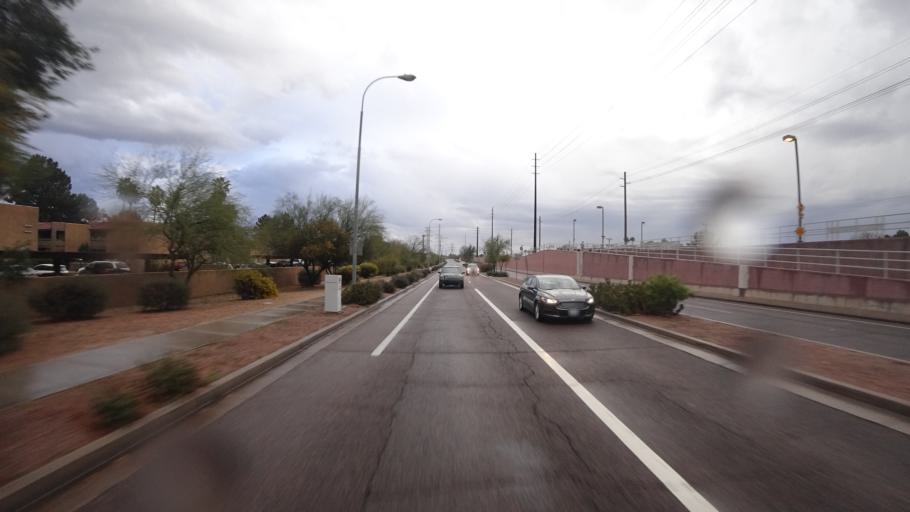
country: US
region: Arizona
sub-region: Maricopa County
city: Paradise Valley
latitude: 33.4872
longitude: -111.9428
